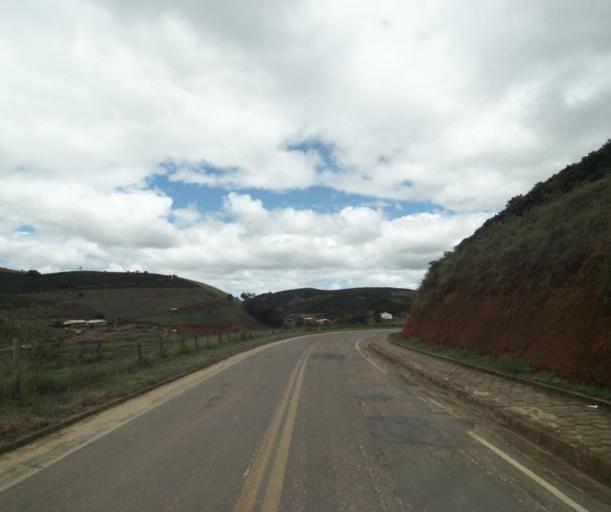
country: BR
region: Espirito Santo
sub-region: Irupi
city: Irupi
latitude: -20.3520
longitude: -41.6266
